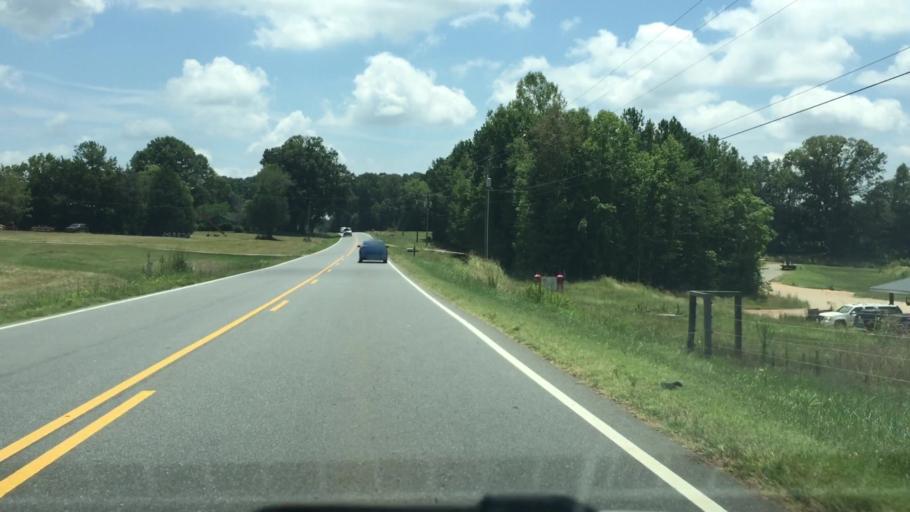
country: US
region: North Carolina
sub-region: Gaston County
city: Davidson
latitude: 35.4851
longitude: -80.7583
